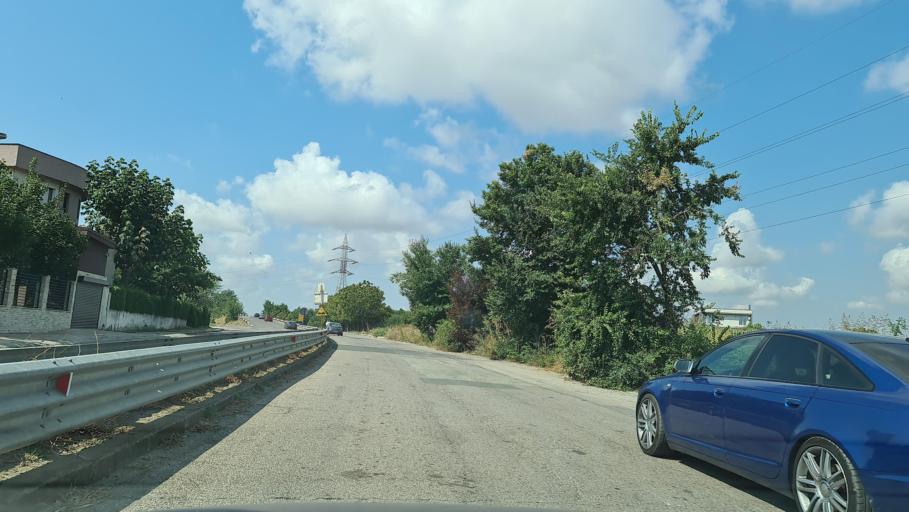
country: RO
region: Constanta
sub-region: Oras Eforie
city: Eforie Nord
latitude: 44.0766
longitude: 28.6299
